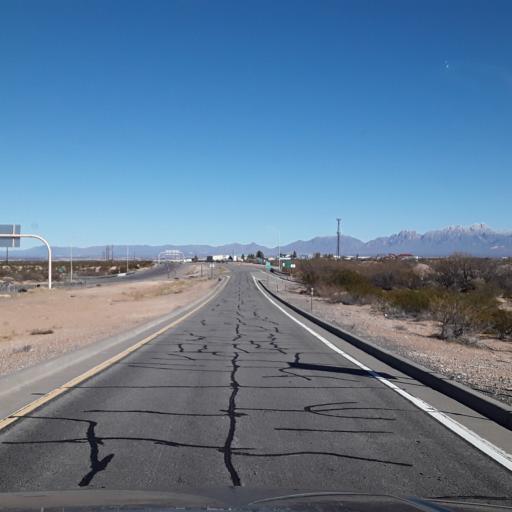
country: US
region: New Mexico
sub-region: Dona Ana County
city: Mesilla
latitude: 32.2831
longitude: -106.8815
